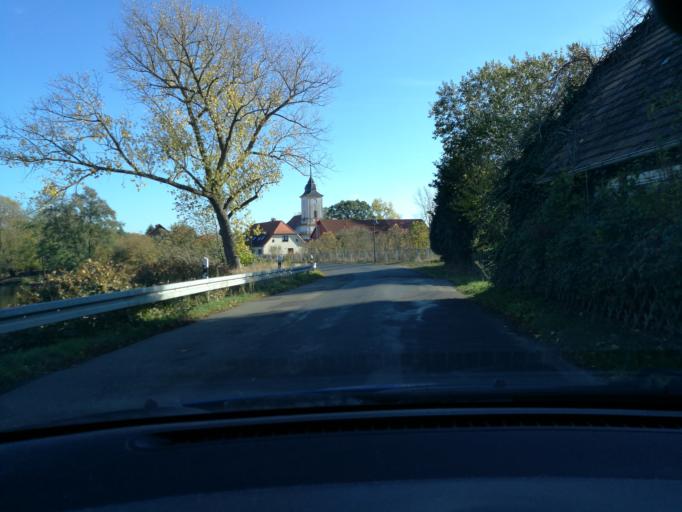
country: DE
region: Brandenburg
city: Lenzen
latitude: 53.1083
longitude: 11.4237
